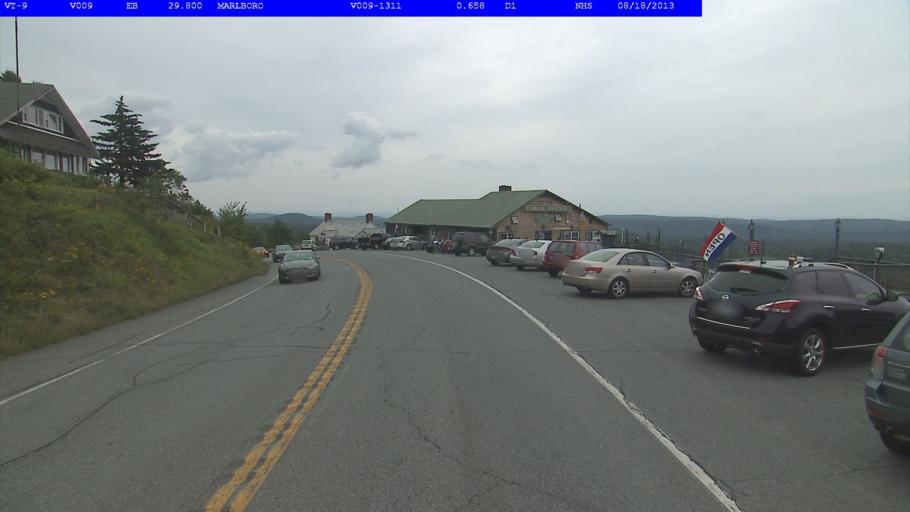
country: US
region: Vermont
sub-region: Windham County
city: Dover
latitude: 42.8528
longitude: -72.7940
